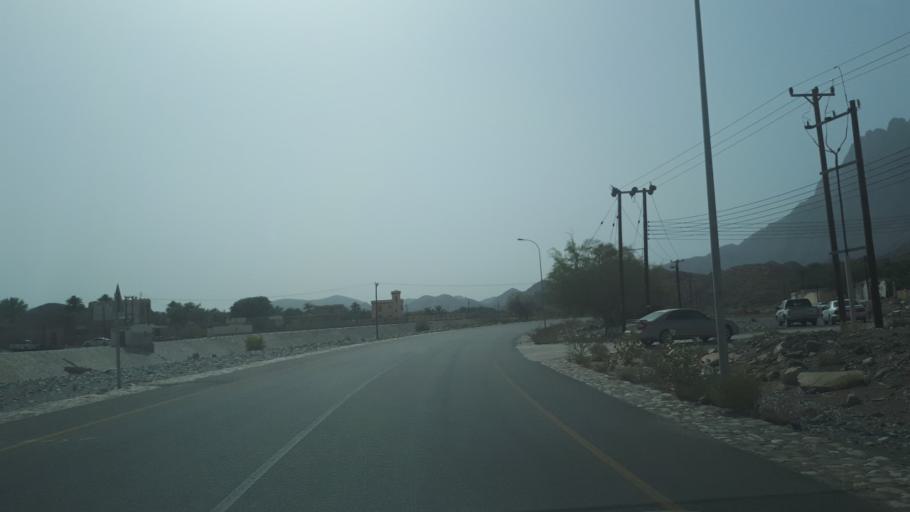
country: OM
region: Muhafazat ad Dakhiliyah
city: Bahla'
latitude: 23.2152
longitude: 57.0160
